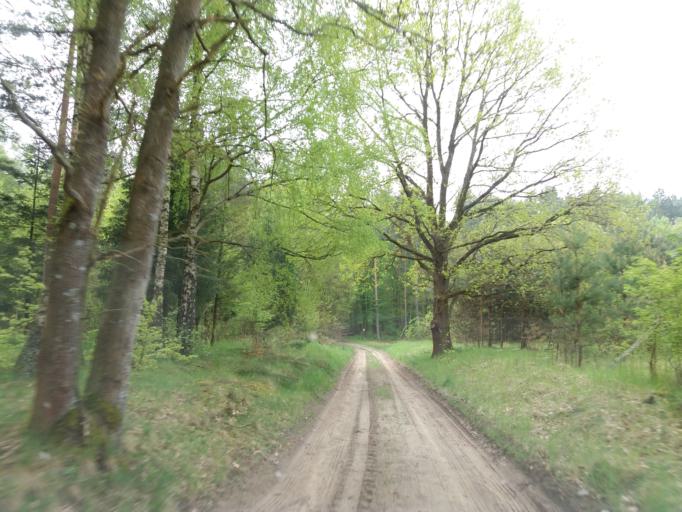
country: PL
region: West Pomeranian Voivodeship
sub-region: Powiat choszczenski
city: Bierzwnik
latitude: 53.0326
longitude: 15.5783
